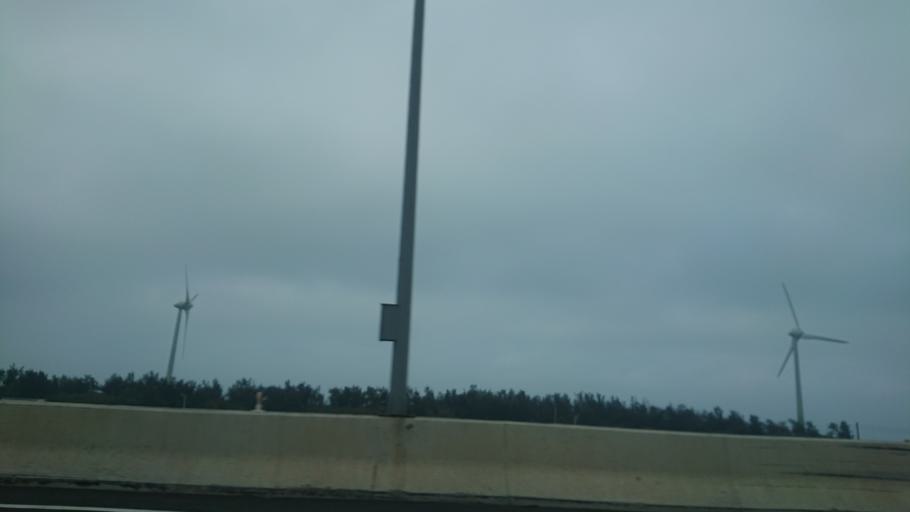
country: TW
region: Taiwan
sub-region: Miaoli
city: Miaoli
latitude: 24.5017
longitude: 120.6788
